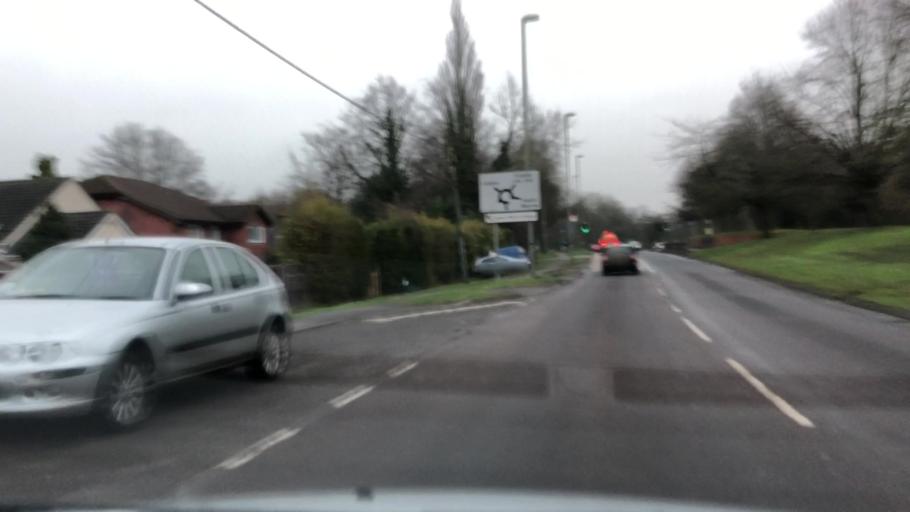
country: GB
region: England
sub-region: Hampshire
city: Basingstoke
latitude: 51.2495
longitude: -1.1016
